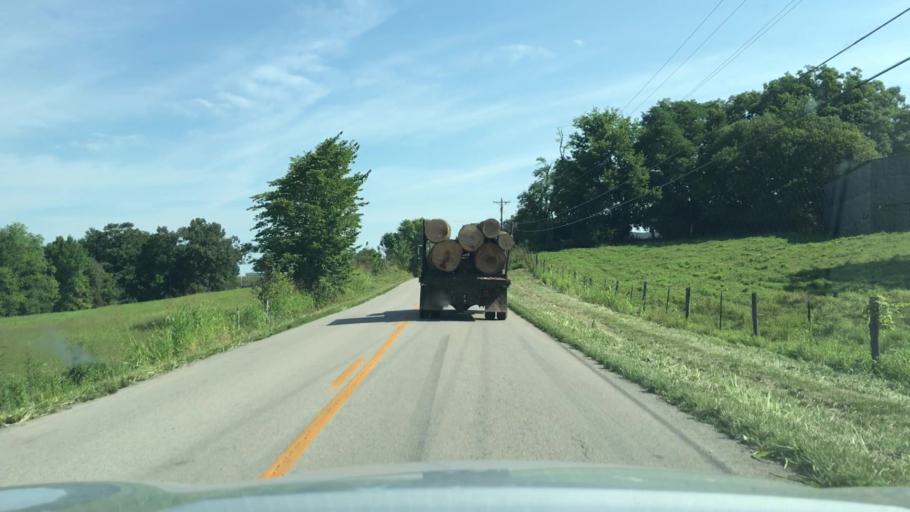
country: US
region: Kentucky
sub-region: Clinton County
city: Albany
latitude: 36.7622
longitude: -84.9970
